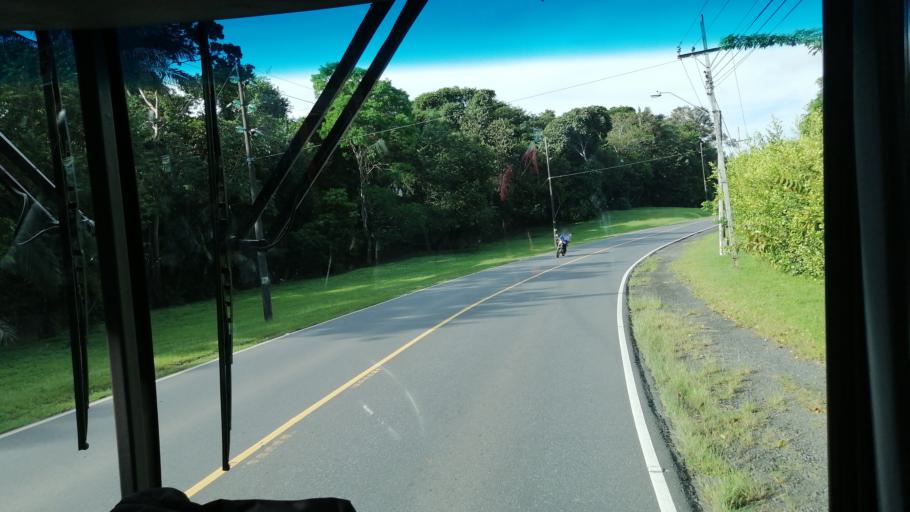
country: PA
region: Panama
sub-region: Distrito de Panama
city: Ancon
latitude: 8.9447
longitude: -79.5917
